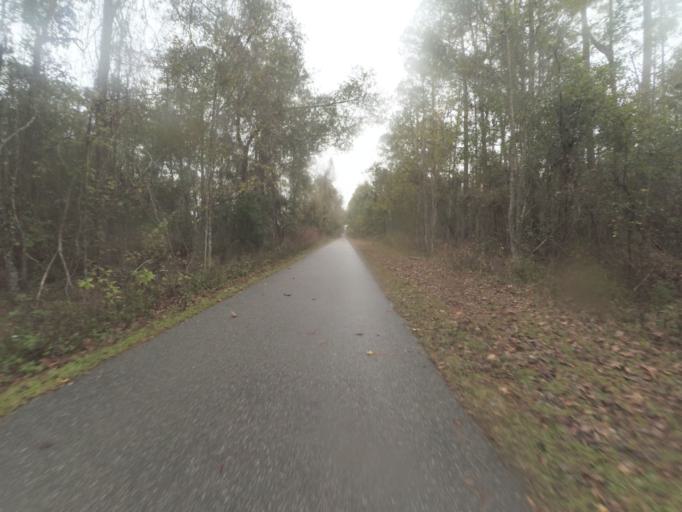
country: US
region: Florida
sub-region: Alachua County
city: Hawthorne
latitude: 29.5876
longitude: -82.0978
